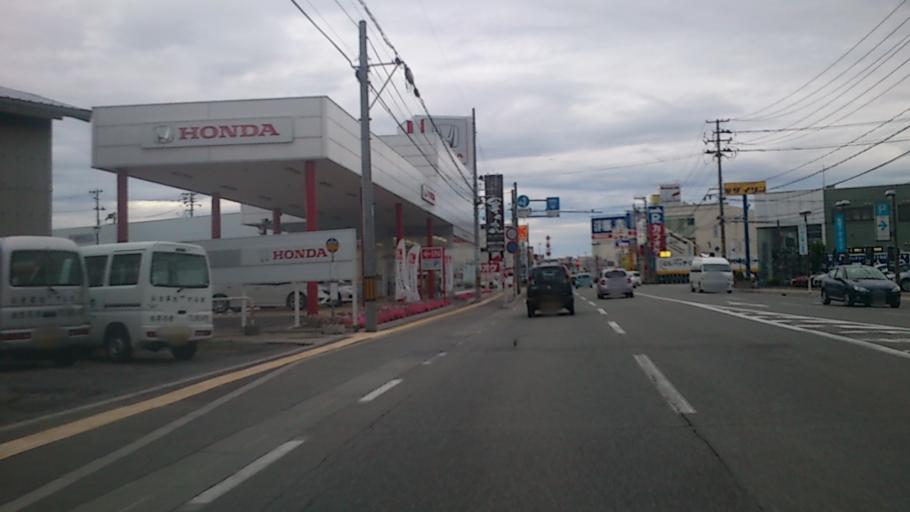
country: JP
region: Akita
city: Akita Shi
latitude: 39.7306
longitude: 140.1033
